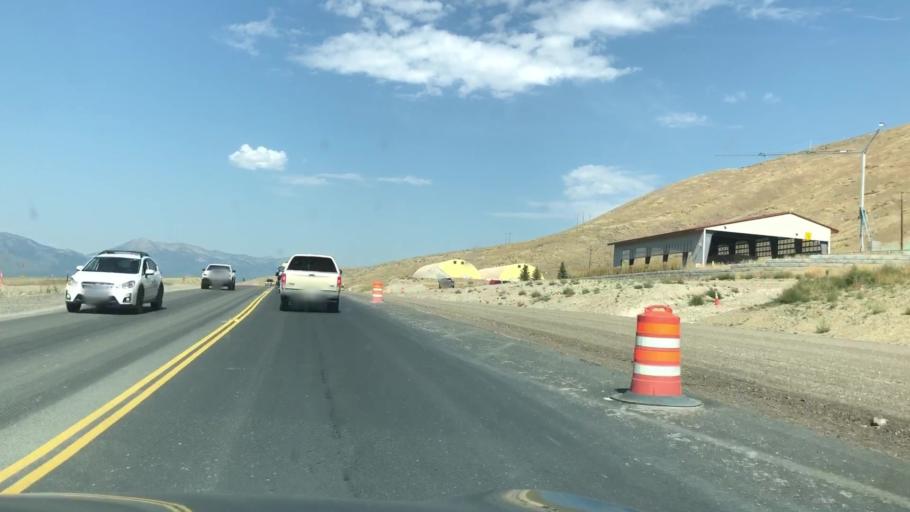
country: US
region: Wyoming
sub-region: Teton County
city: South Park
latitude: 43.4000
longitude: -110.7522
